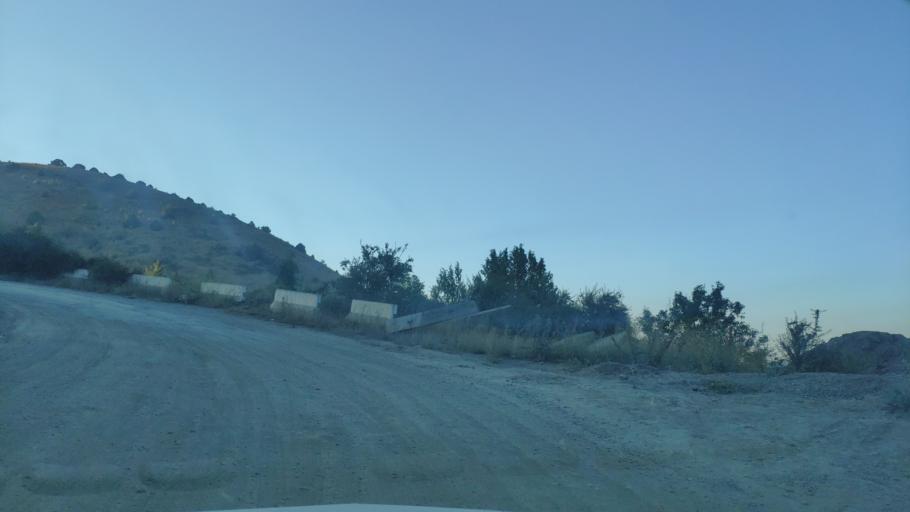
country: TJ
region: Viloyati Sughd
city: Ayni
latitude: 39.6409
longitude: 68.4714
